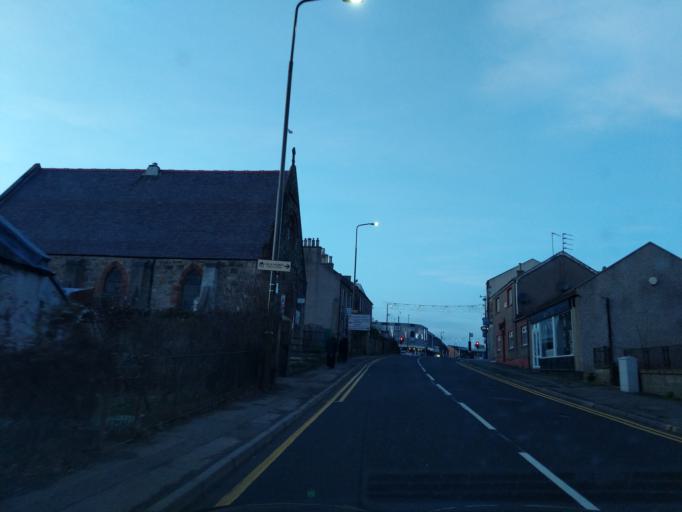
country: GB
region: Scotland
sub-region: Midlothian
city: Bonnyrigg
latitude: 55.8741
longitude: -3.1043
